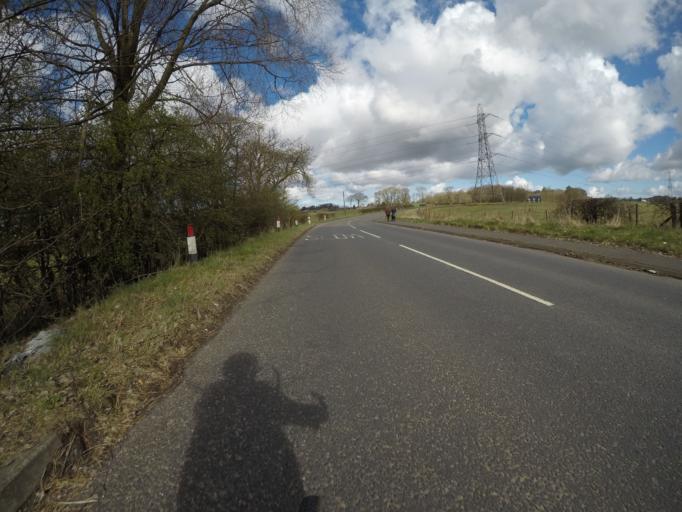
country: GB
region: Scotland
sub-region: North Ayrshire
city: Beith
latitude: 55.7401
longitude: -4.6254
